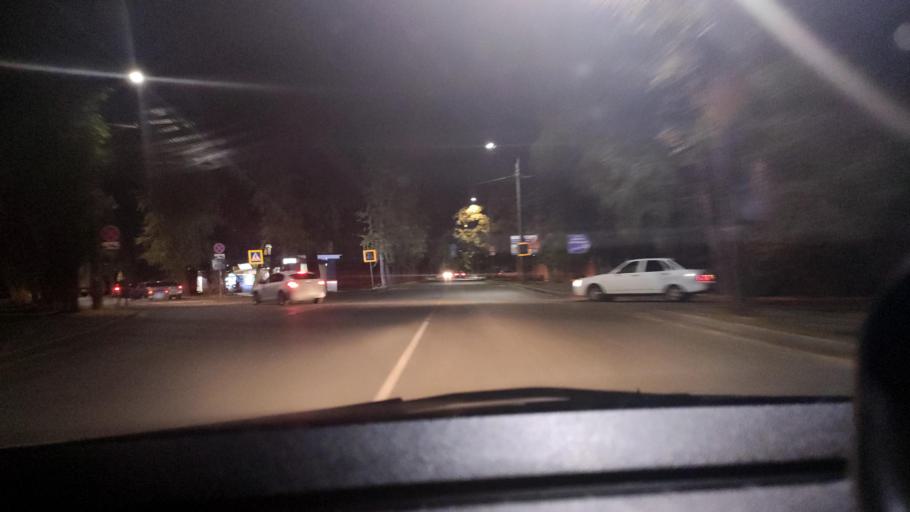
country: RU
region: Voronezj
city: Voronezh
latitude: 51.6852
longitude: 39.1808
